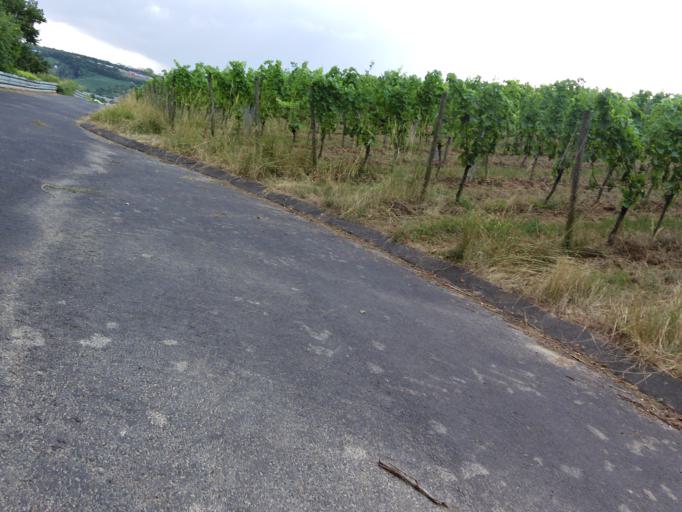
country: DE
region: Bavaria
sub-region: Regierungsbezirk Unterfranken
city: Randersacker
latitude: 49.7633
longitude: 9.9805
